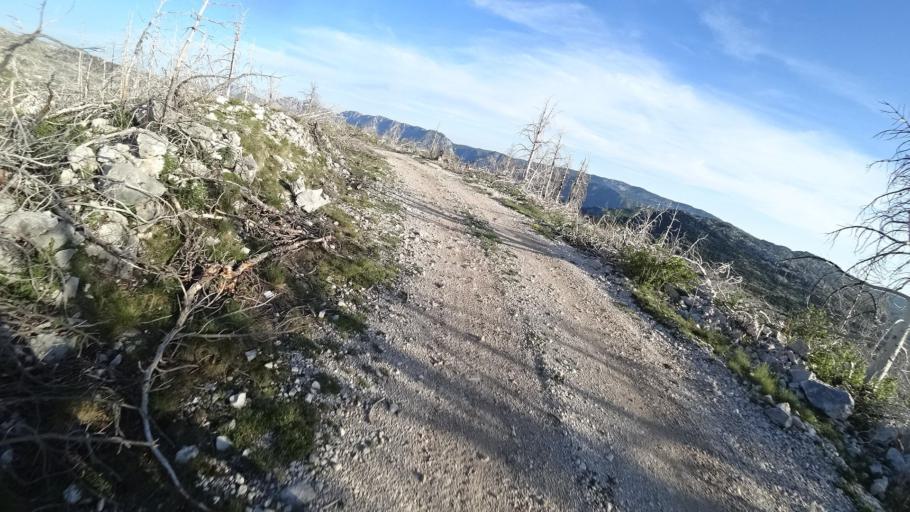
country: BA
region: Federation of Bosnia and Herzegovina
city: Kocerin
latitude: 43.5789
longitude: 17.5403
